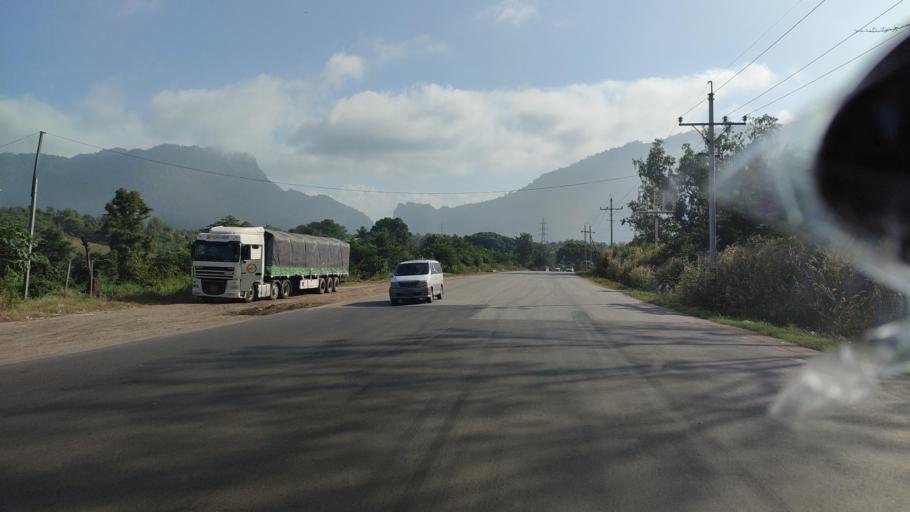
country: MM
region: Mandalay
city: Yamethin
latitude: 20.8176
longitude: 96.3860
